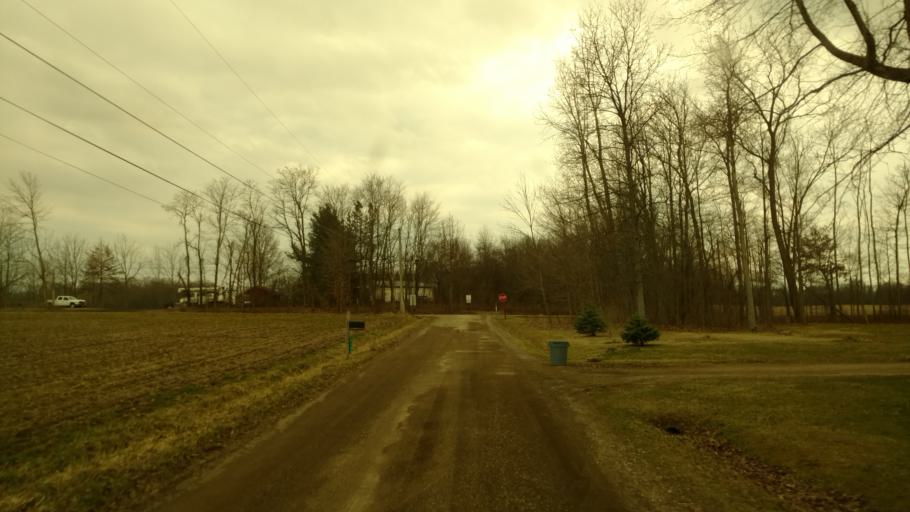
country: US
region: Ohio
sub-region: Richland County
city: Lexington
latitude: 40.6821
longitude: -82.6764
